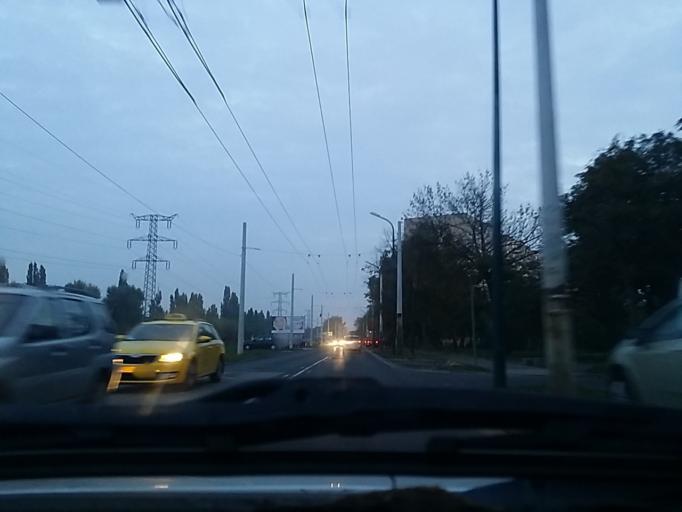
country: HU
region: Budapest
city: Budapest XVI. keruelet
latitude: 47.5159
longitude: 19.1436
